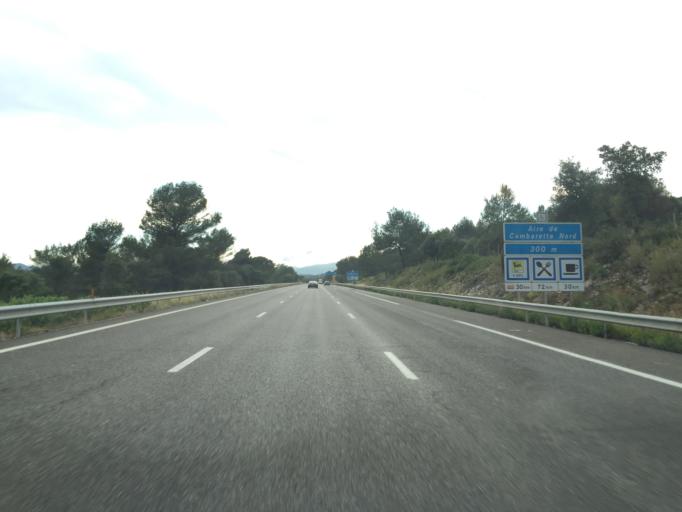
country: FR
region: Provence-Alpes-Cote d'Azur
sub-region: Departement du Var
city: La Celle
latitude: 43.4224
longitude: 6.0022
